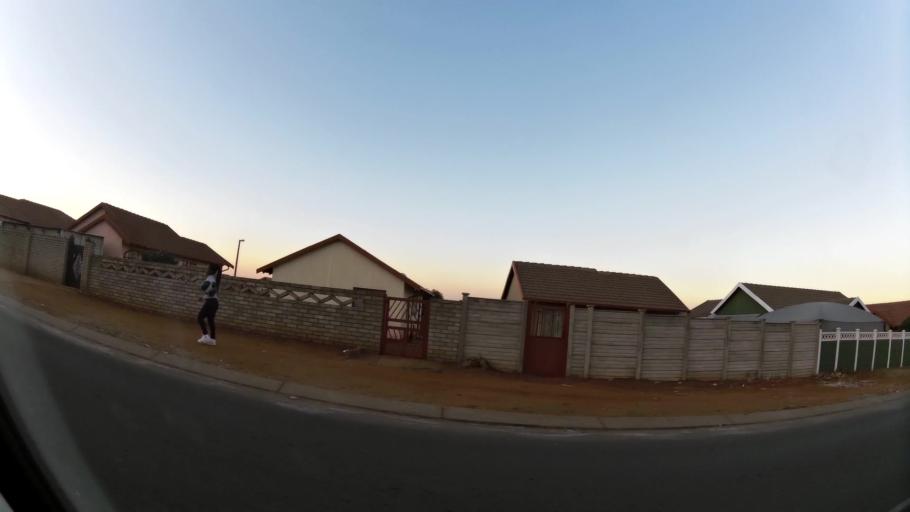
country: ZA
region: North-West
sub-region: Bojanala Platinum District Municipality
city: Rustenburg
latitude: -25.6525
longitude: 27.2073
